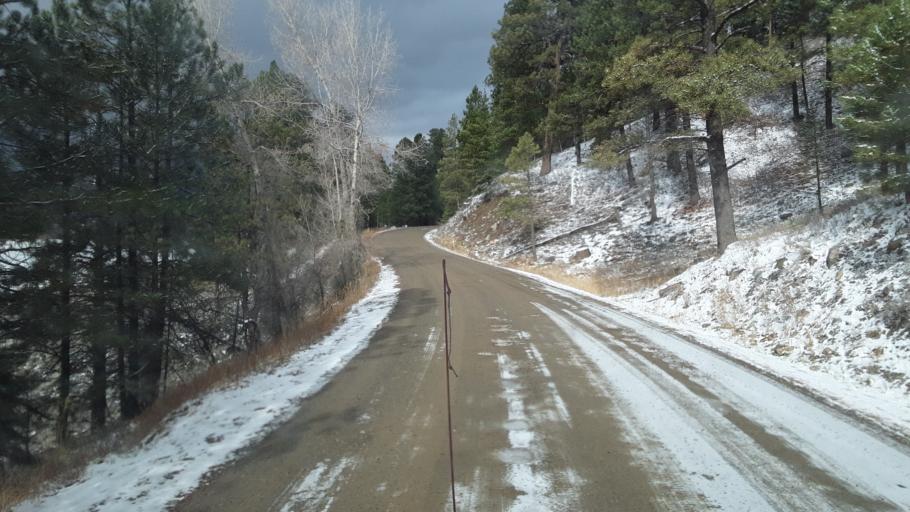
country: US
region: Colorado
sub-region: La Plata County
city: Bayfield
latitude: 37.4222
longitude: -107.5370
